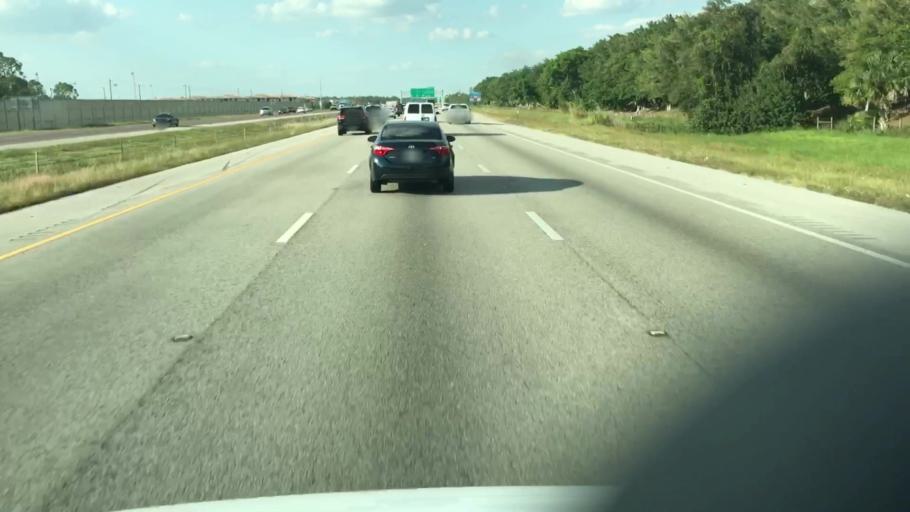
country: US
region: Florida
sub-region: Lee County
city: Three Oaks
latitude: 26.4744
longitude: -81.7908
